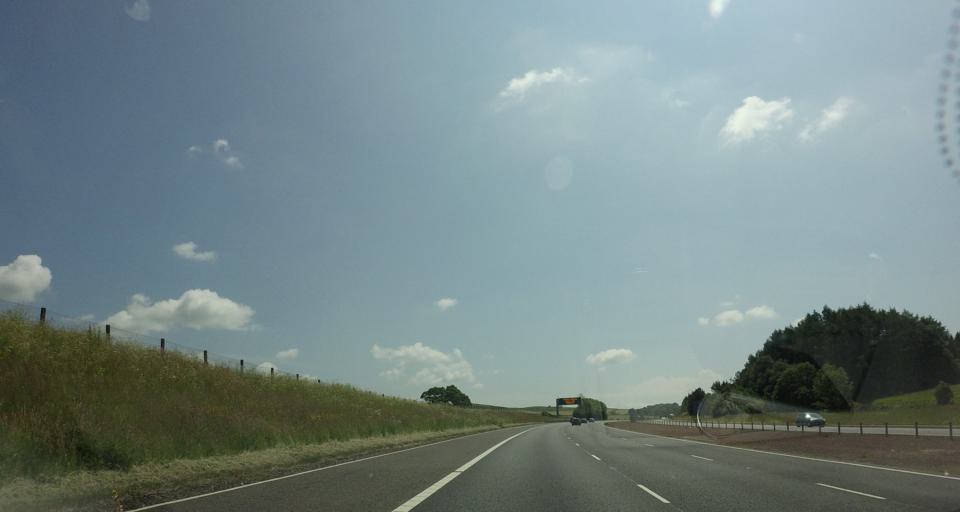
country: GB
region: Scotland
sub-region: Dumfries and Galloway
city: Lockerbie
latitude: 55.0935
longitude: -3.3228
